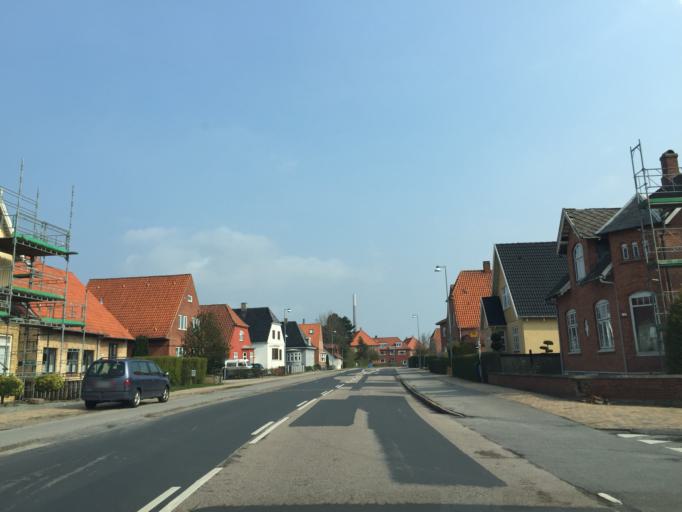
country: DK
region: South Denmark
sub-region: Odense Kommune
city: Odense
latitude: 55.4154
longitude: 10.3975
